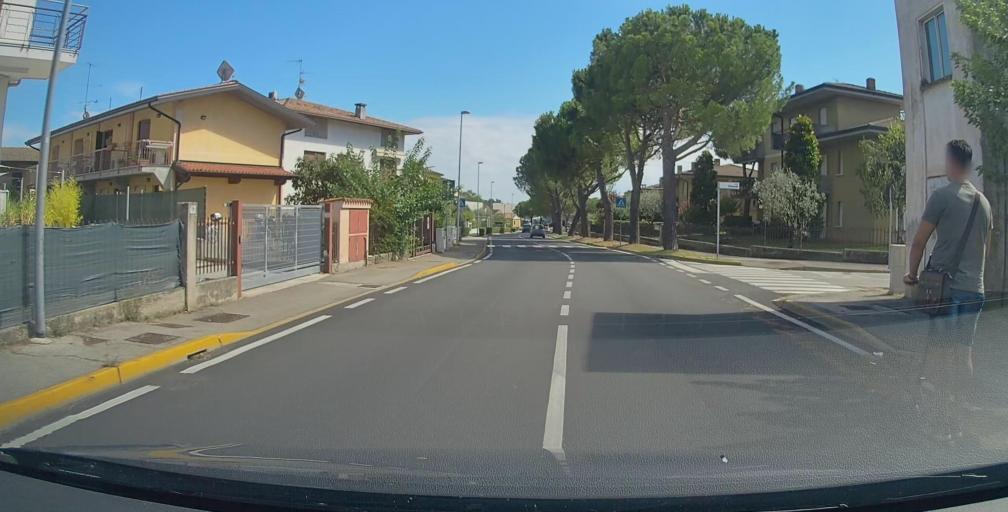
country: IT
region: Lombardy
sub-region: Provincia di Brescia
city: San Martino della Battaglia
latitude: 45.4611
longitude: 10.6073
